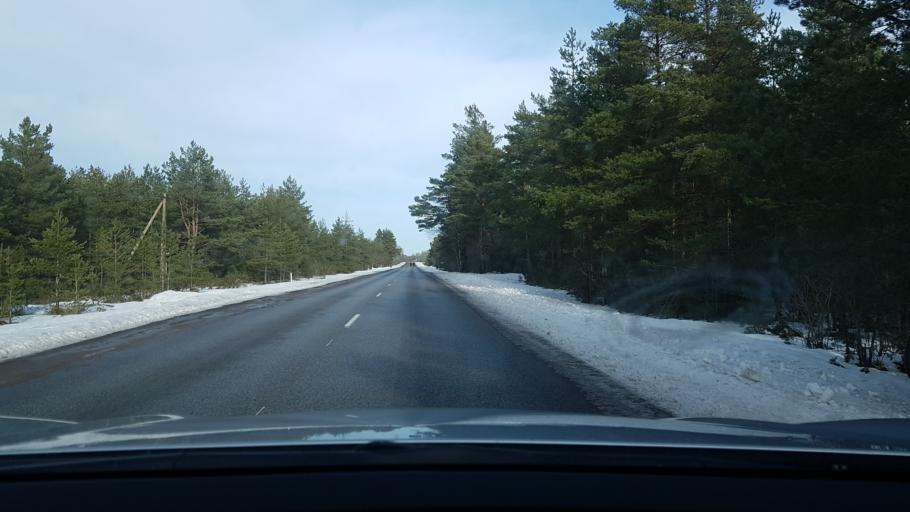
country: EE
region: Saare
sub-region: Kuressaare linn
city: Kuressaare
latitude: 58.3212
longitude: 22.5495
